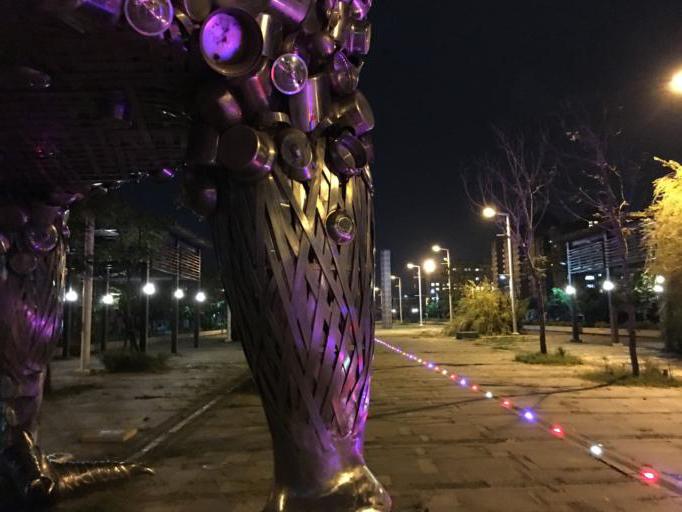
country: TW
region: Taiwan
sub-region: Chiayi
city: Taibao
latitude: 23.4684
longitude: 120.2941
